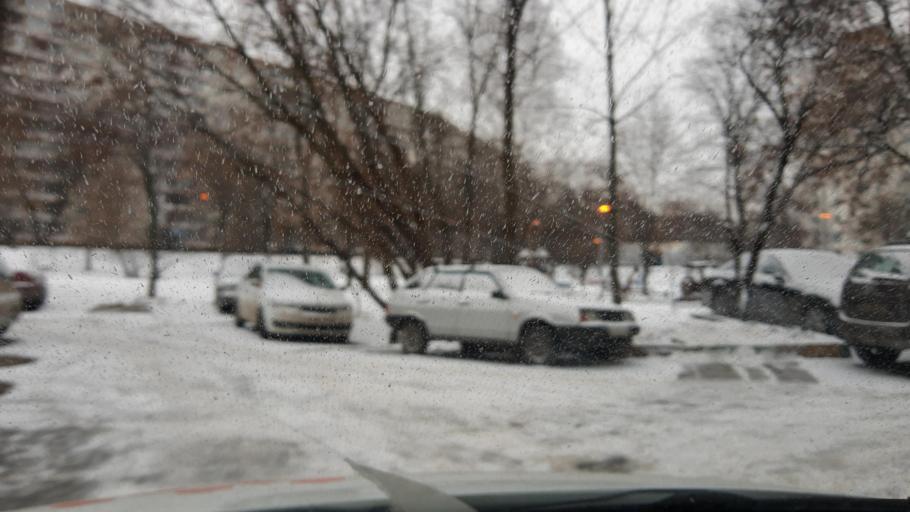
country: RU
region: Moskovskaya
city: Biryulevo Zapadnoye
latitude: 55.5828
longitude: 37.6537
